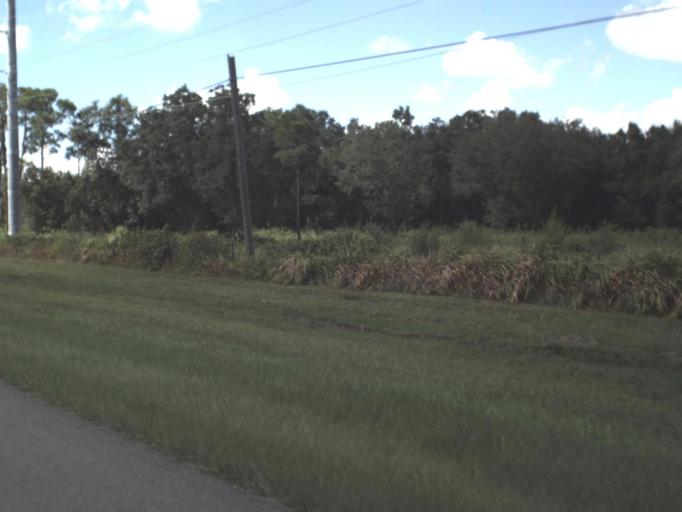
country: US
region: Florida
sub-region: Sarasota County
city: The Meadows
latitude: 27.4169
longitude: -82.3567
